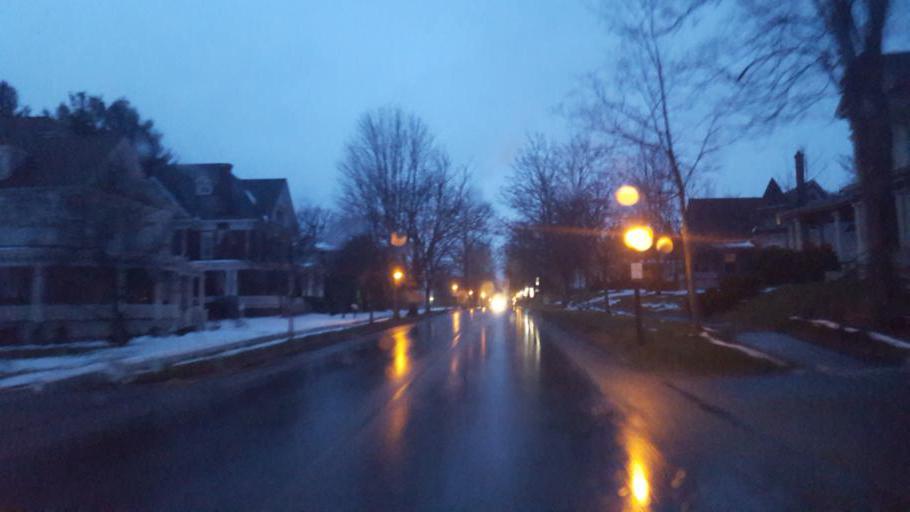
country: US
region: Pennsylvania
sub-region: McKean County
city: Smethport
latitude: 41.8095
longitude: -78.4490
